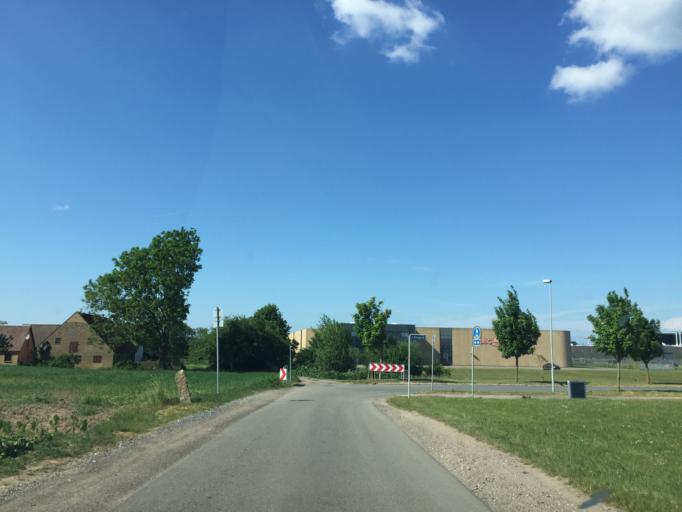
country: DK
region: South Denmark
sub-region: Odense Kommune
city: Hojby
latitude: 55.3445
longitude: 10.3973
